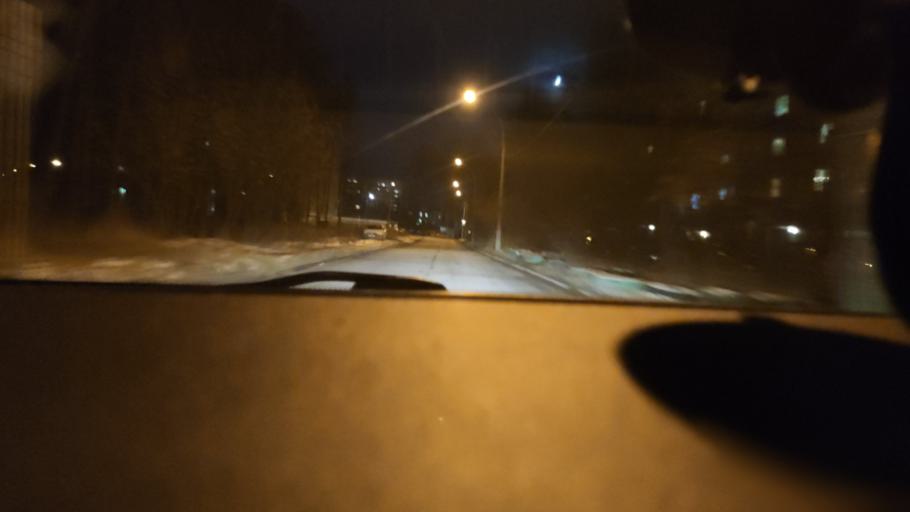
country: RU
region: Perm
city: Kondratovo
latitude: 58.0289
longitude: 56.0119
